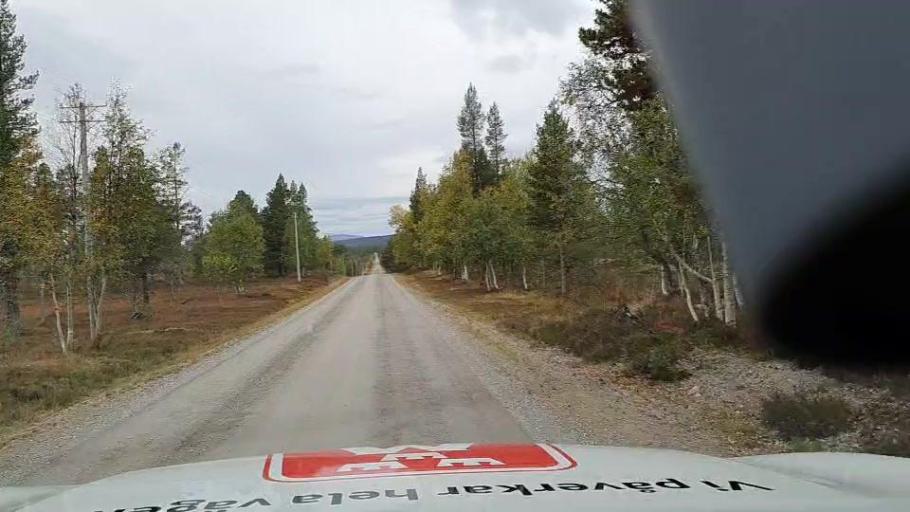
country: NO
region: Hedmark
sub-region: Engerdal
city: Engerdal
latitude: 62.0935
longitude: 12.8118
